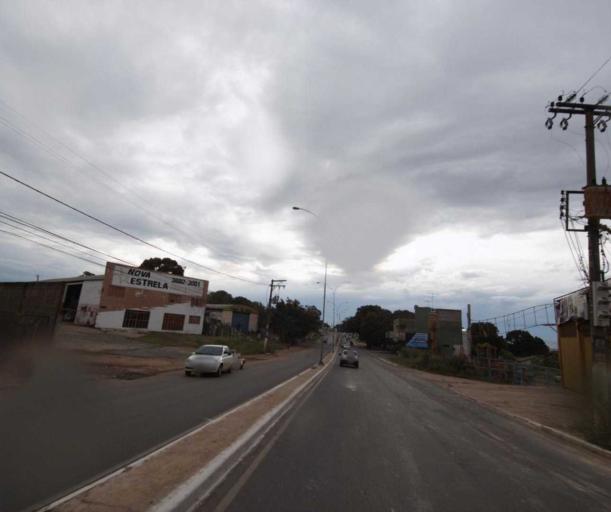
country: BR
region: Mato Grosso
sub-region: Varzea Grande
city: Varzea Grande
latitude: -15.6456
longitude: -56.1401
